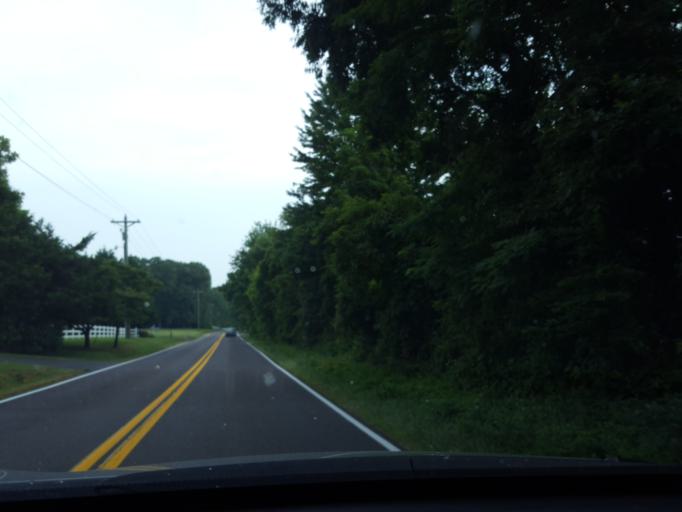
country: US
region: Virginia
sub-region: Orange County
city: Orange
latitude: 38.2702
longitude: -77.8934
